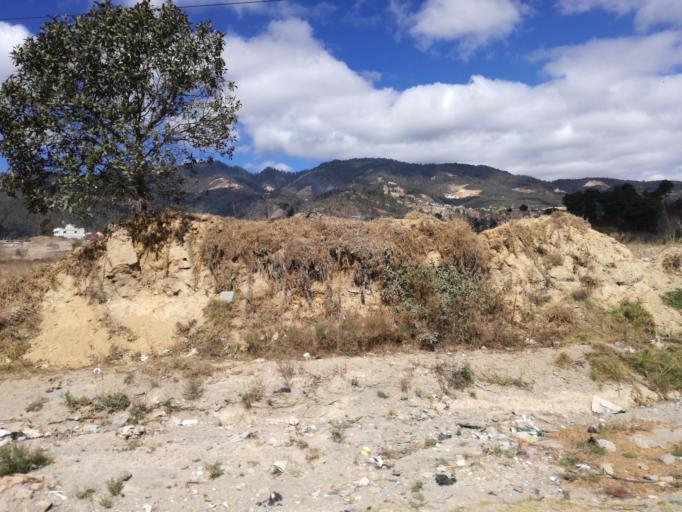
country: GT
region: Quetzaltenango
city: Quetzaltenango
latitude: 14.8032
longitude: -91.5421
